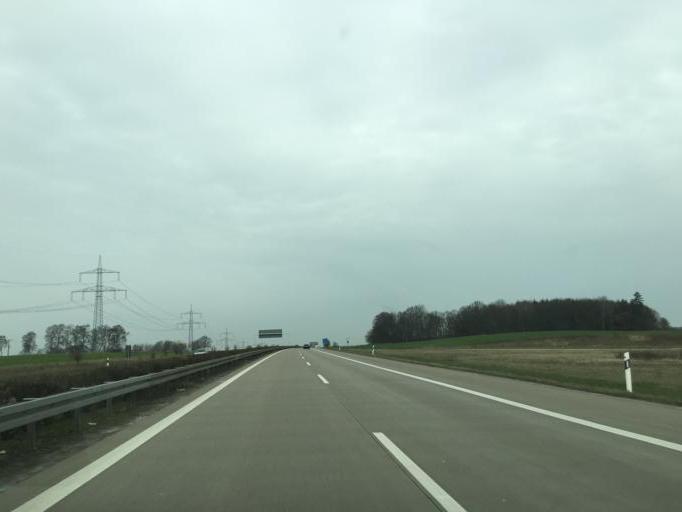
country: DE
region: Mecklenburg-Vorpommern
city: Kavelstorf
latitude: 54.0360
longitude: 12.1992
